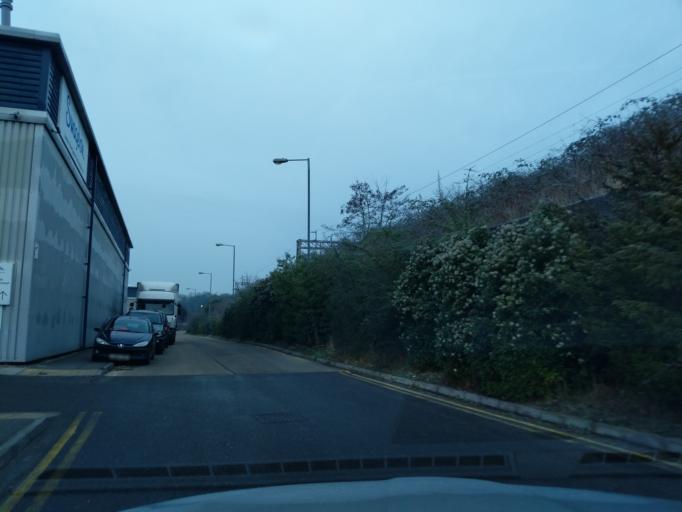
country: GB
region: England
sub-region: Hertfordshire
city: Kings Langley
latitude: 51.7115
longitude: -0.4400
